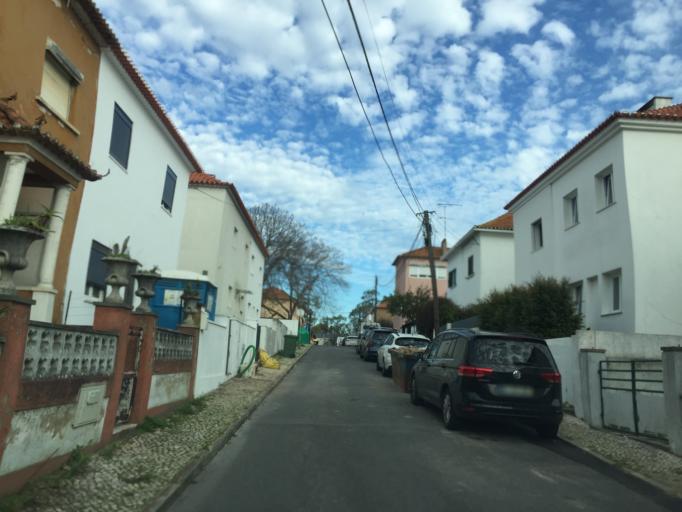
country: PT
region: Lisbon
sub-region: Oeiras
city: Alges
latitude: 38.7158
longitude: -9.2176
